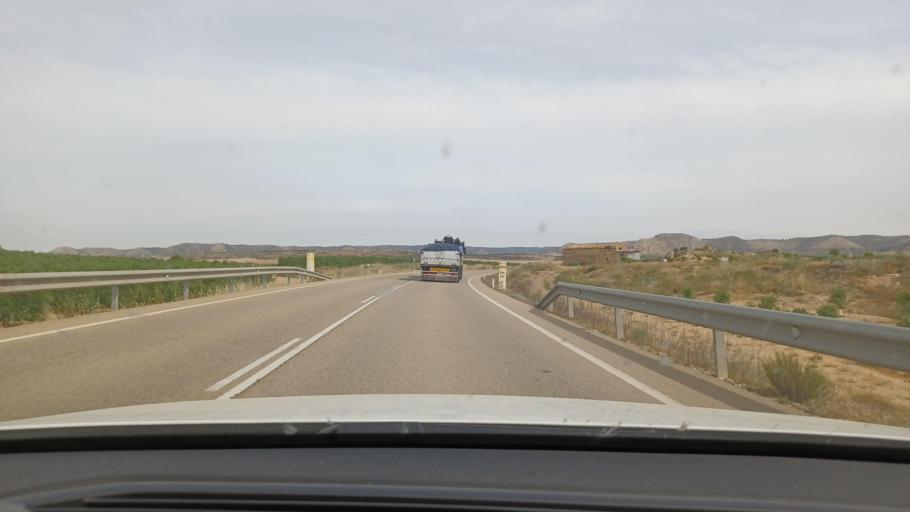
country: ES
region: Aragon
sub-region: Provincia de Zaragoza
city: Chiprana
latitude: 41.3076
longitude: -0.0729
